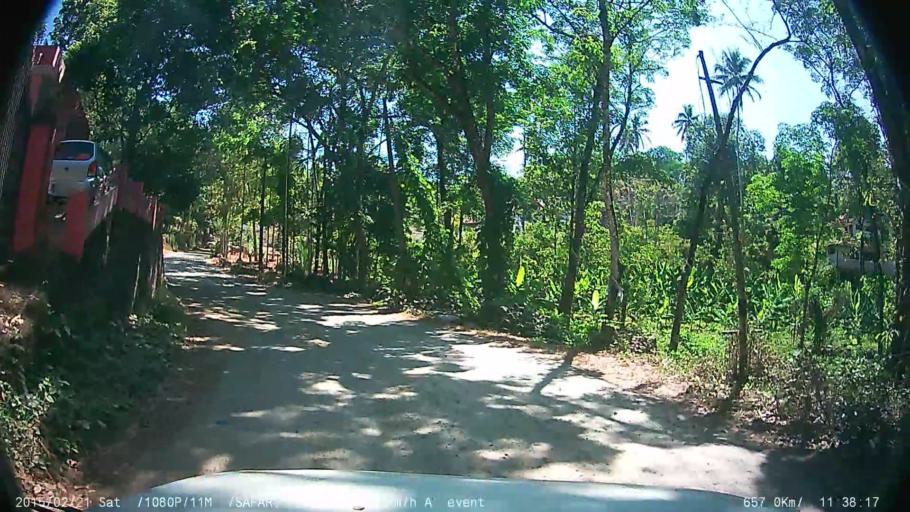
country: IN
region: Kerala
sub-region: Kottayam
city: Lalam
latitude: 9.8064
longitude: 76.7302
